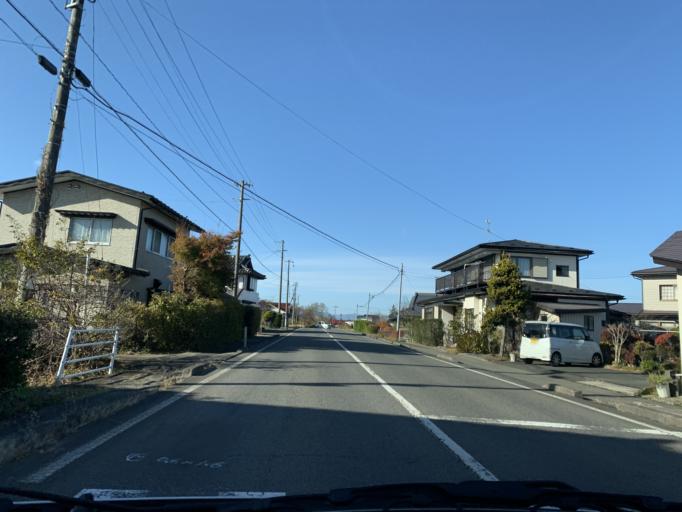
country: JP
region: Iwate
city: Mizusawa
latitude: 39.1818
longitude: 141.1311
